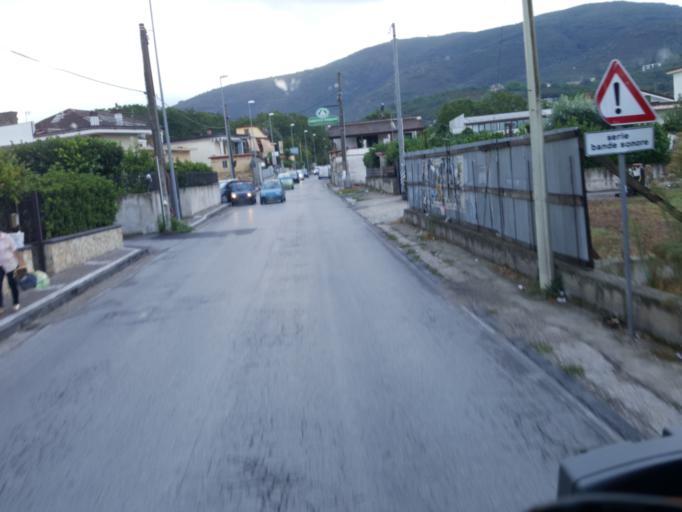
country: IT
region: Campania
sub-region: Provincia di Napoli
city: Palma Campania
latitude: 40.8788
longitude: 14.5572
